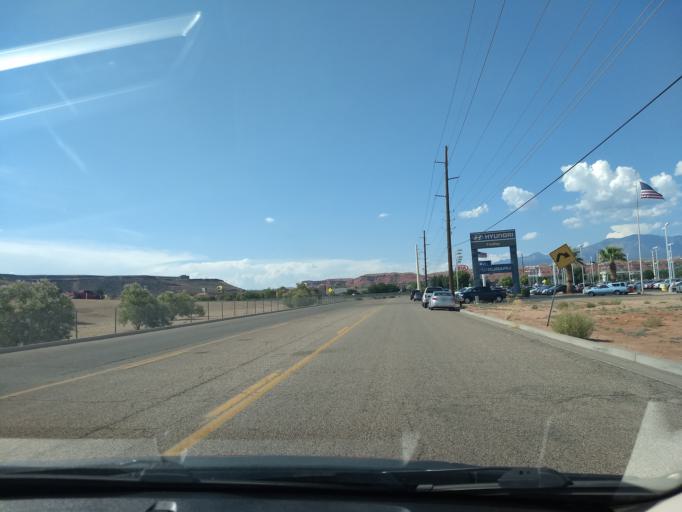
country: US
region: Utah
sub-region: Washington County
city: Saint George
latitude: 37.0833
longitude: -113.5810
